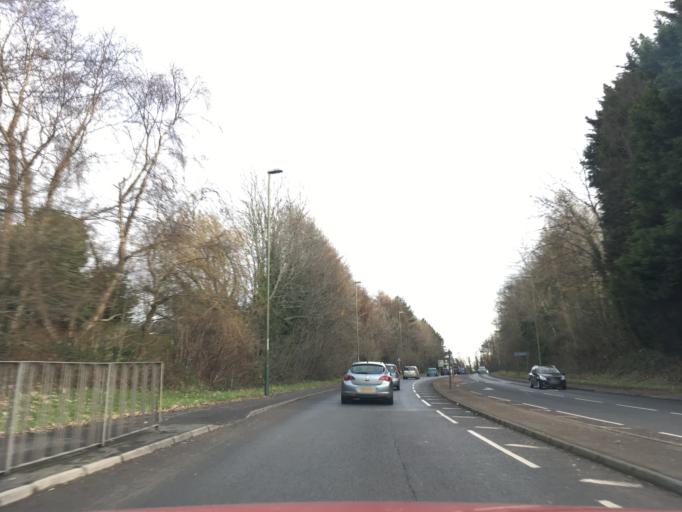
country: GB
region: Wales
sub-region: Caerphilly County Borough
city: Bedwas
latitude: 51.5895
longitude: -3.1989
